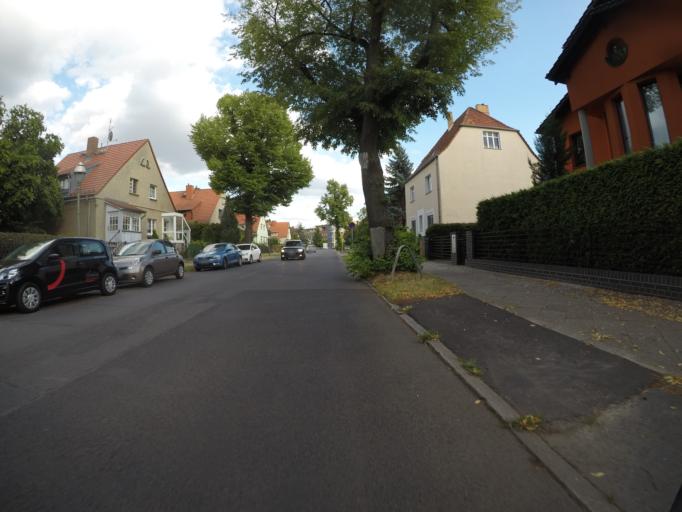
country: DE
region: Berlin
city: Kaulsdorf
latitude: 52.5085
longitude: 13.5906
